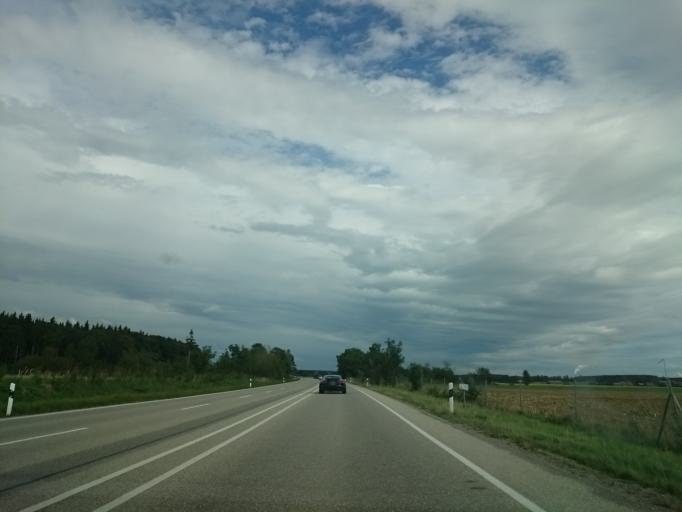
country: DE
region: Bavaria
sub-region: Swabia
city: Rieden
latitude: 47.9583
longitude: 10.6821
